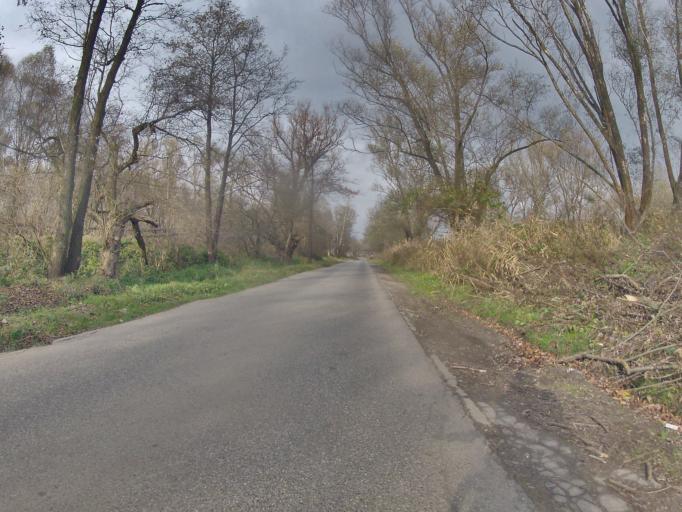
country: PL
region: Lesser Poland Voivodeship
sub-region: Powiat wielicki
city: Wegrzce Wielkie
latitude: 50.0596
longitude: 20.1023
